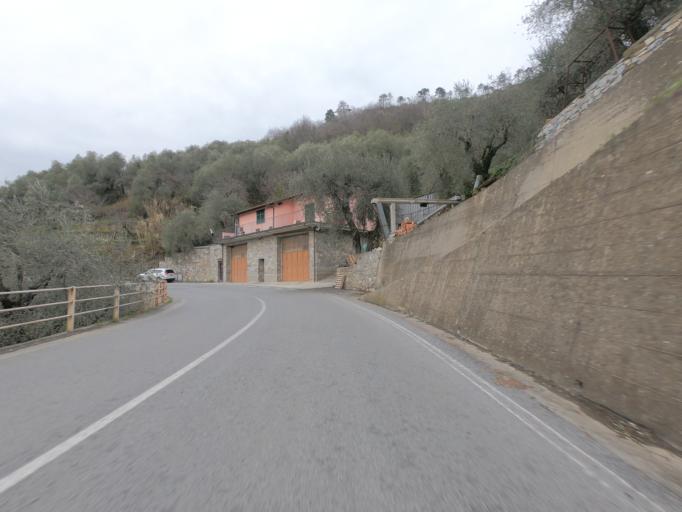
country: IT
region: Liguria
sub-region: Provincia di Savona
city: Casanova Lerrone
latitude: 44.0316
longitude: 8.0391
